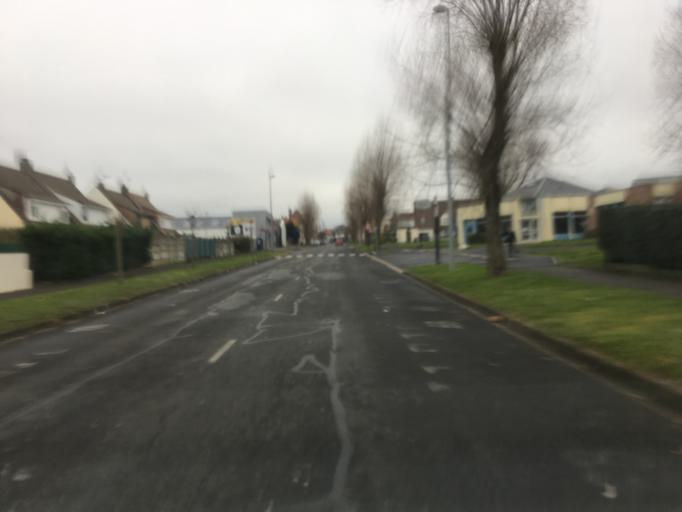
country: FR
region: Nord-Pas-de-Calais
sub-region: Departement du Pas-de-Calais
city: Outreau
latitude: 50.7088
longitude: 1.5862
